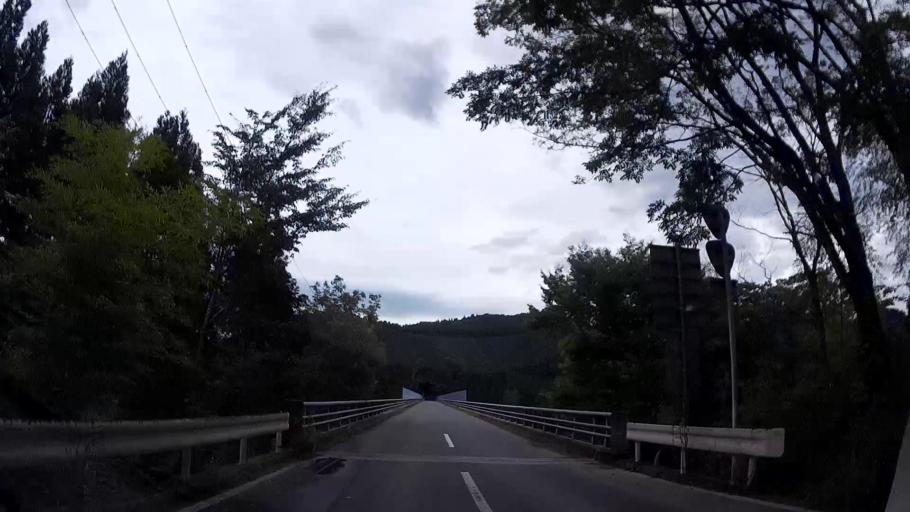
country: JP
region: Oita
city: Hita
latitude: 33.1399
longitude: 130.9756
